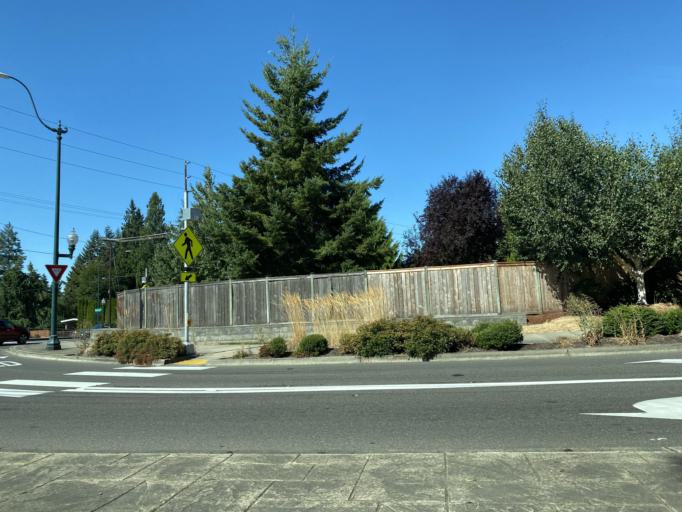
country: US
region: Washington
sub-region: Thurston County
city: Tumwater
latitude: 47.0043
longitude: -122.8653
